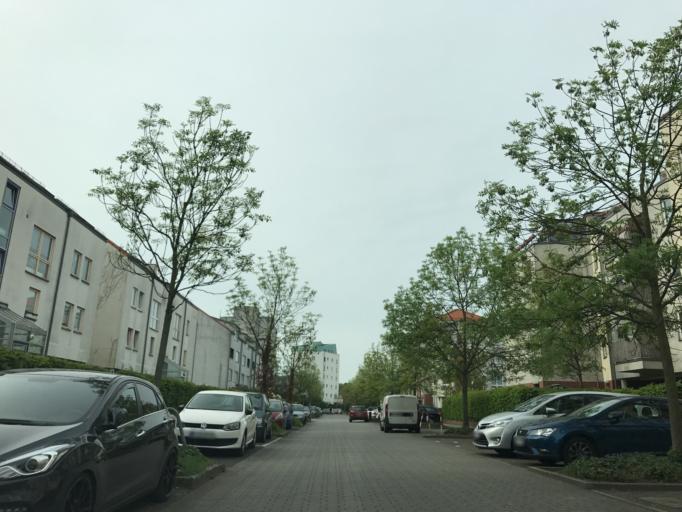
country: DE
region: Berlin
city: Staaken
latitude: 52.5267
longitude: 13.1492
